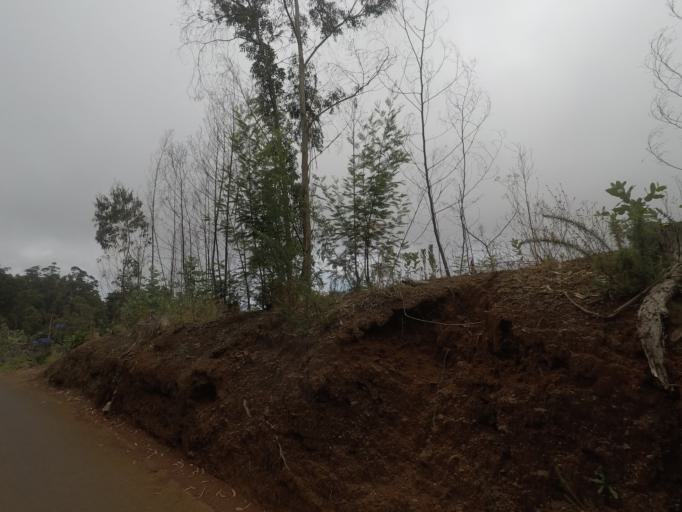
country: PT
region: Madeira
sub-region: Funchal
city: Nossa Senhora do Monte
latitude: 32.6708
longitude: -16.8799
